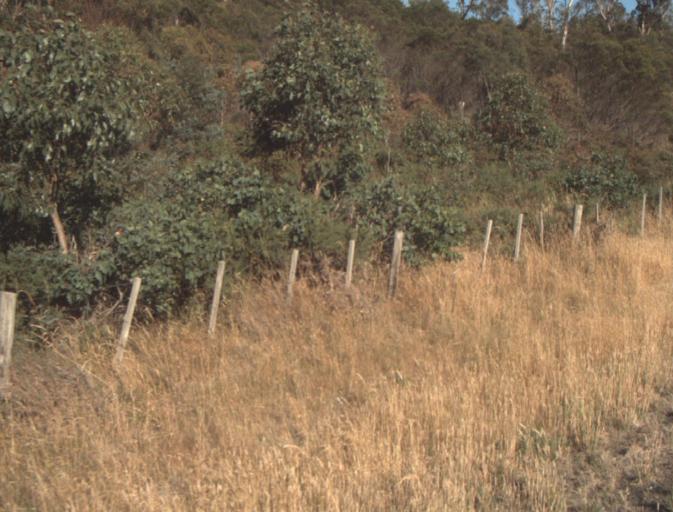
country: AU
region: Tasmania
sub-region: Launceston
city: Newstead
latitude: -41.4369
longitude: 147.2532
